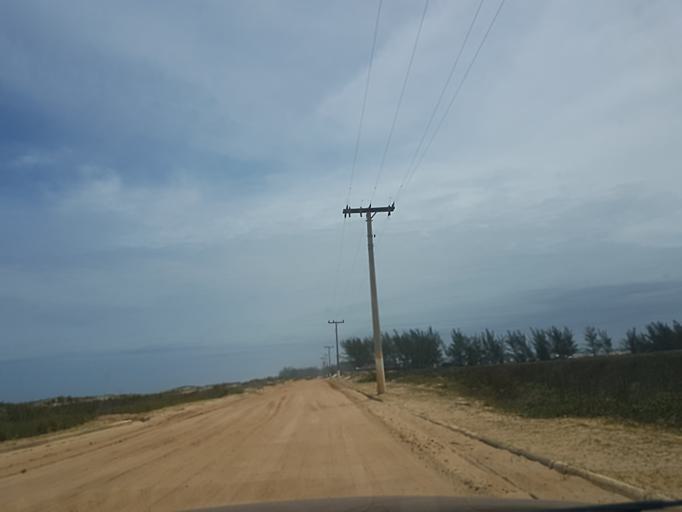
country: BR
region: Santa Catarina
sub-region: Jaguaruna
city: Jaguaruna
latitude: -28.6673
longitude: -48.9686
